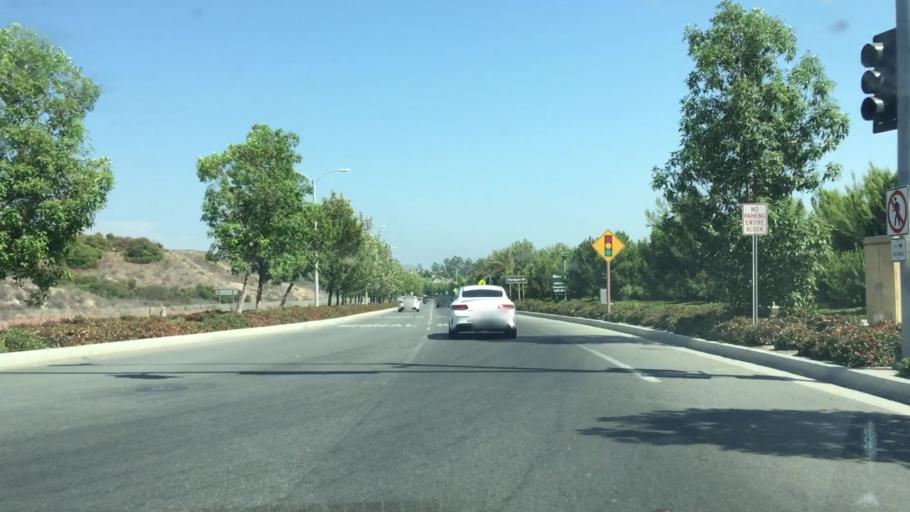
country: US
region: California
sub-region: Orange County
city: North Tustin
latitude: 33.7114
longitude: -117.7379
